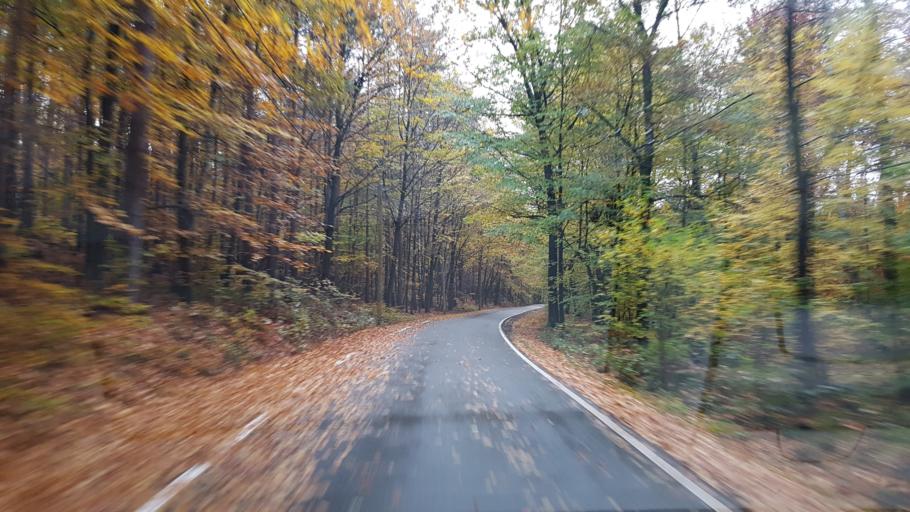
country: DE
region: Saxony
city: Cavertitz
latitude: 51.4101
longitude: 13.0668
